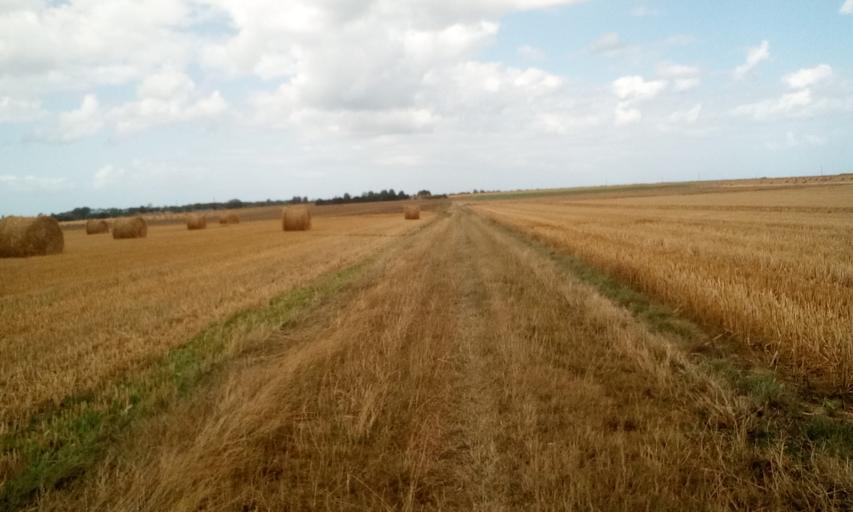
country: FR
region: Lower Normandy
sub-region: Departement du Calvados
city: Ver-sur-Mer
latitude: 49.3169
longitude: -0.5300
